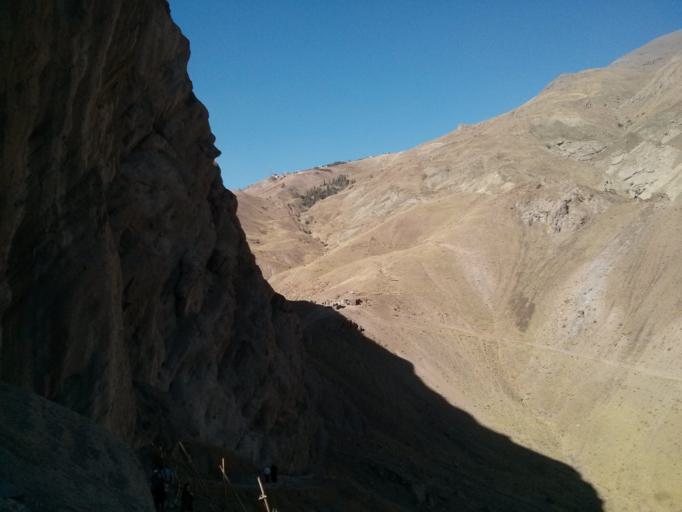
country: IR
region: Alborz
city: Shahrak
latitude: 36.4462
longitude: 50.5857
